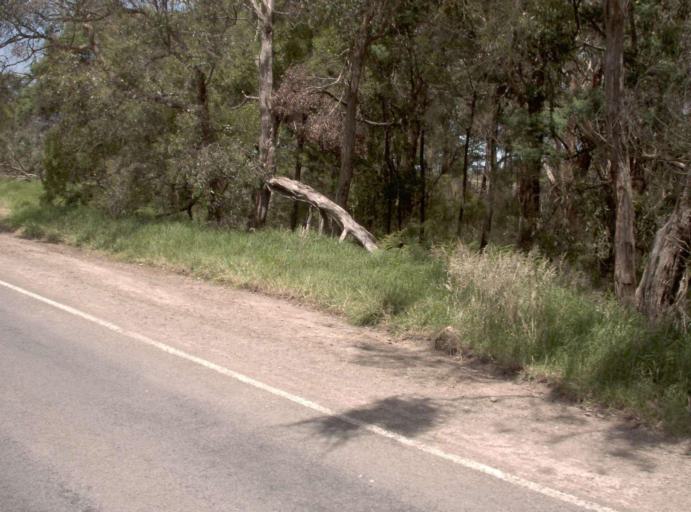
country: AU
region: Victoria
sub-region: Bass Coast
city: North Wonthaggi
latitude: -38.6479
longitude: 146.0104
